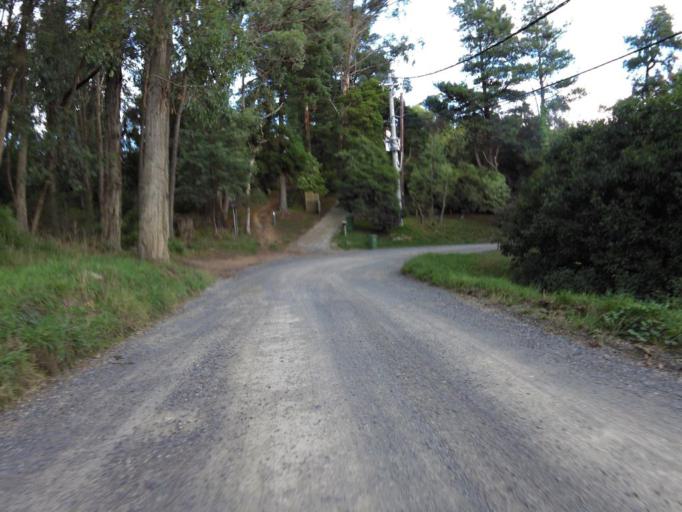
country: AU
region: Victoria
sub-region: Yarra Ranges
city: Mount Evelyn
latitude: -37.8016
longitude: 145.3972
